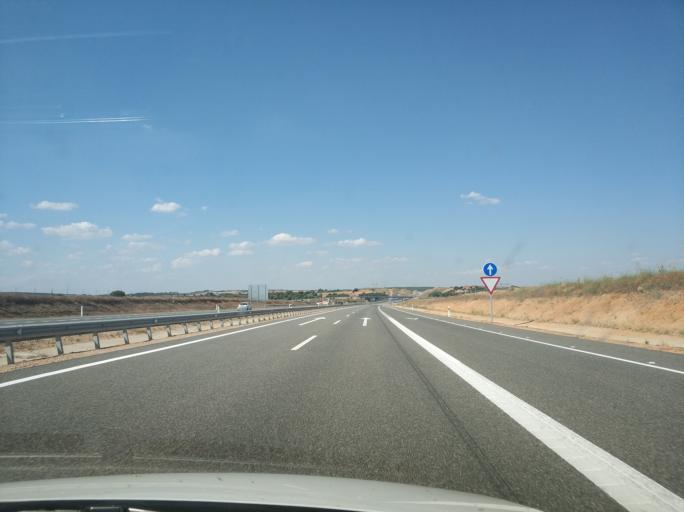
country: ES
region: Castille and Leon
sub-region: Provincia de Zamora
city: Granja de Moreruela
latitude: 41.8020
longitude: -5.7547
